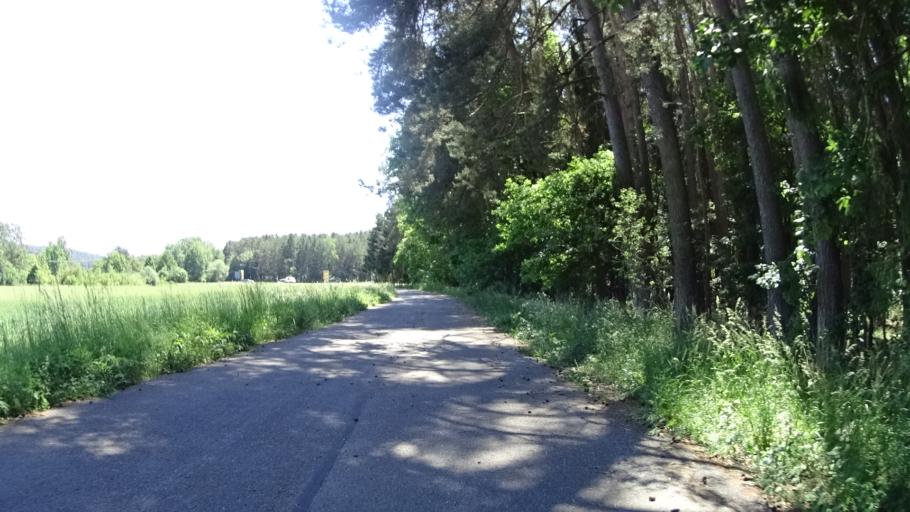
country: DE
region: Bavaria
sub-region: Regierungsbezirk Mittelfranken
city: Absberg
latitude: 49.1095
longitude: 10.9224
